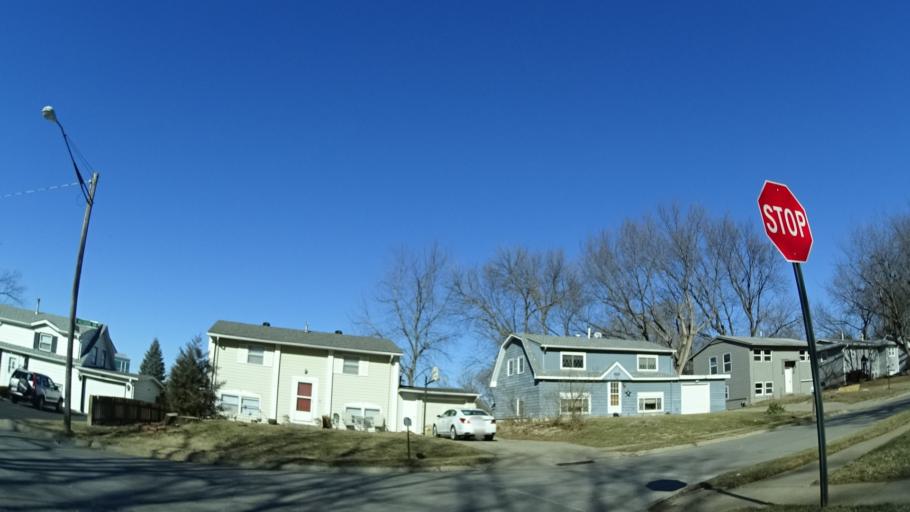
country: US
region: Nebraska
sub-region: Sarpy County
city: Offutt Air Force Base
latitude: 41.1466
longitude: -95.9183
